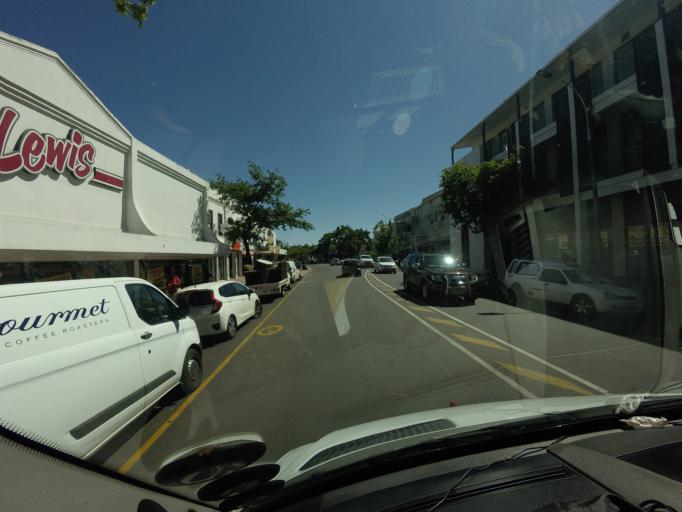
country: ZA
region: Western Cape
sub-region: Cape Winelands District Municipality
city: Stellenbosch
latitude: -33.9345
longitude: 18.8592
